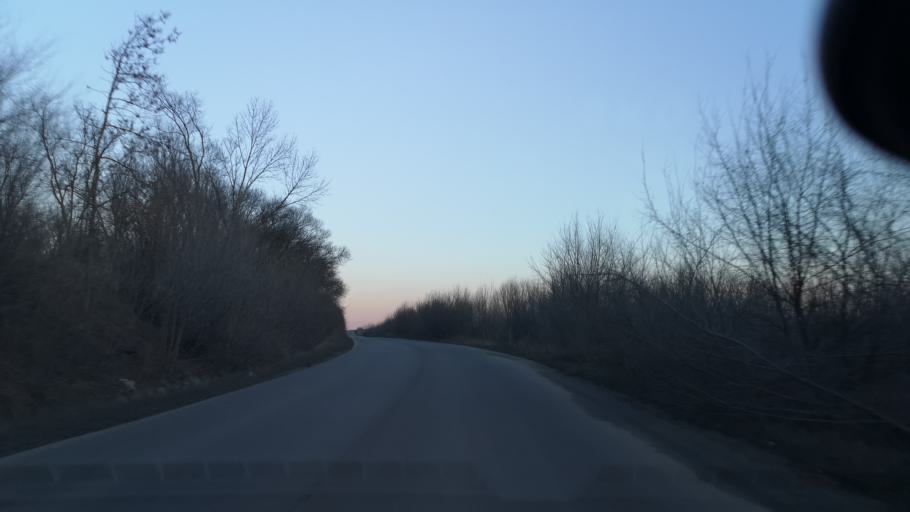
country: MD
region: Anenii Noi
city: Anenii Noi
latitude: 46.8880
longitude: 29.2662
